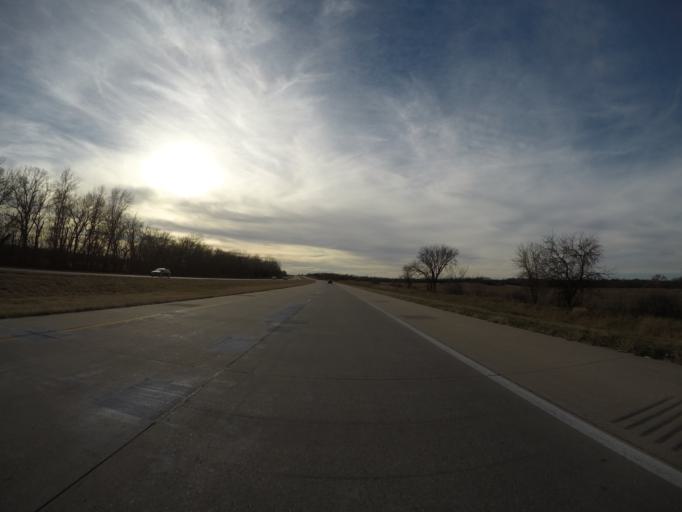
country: US
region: Kansas
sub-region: Franklin County
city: Ottawa
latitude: 38.5560
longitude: -95.3431
